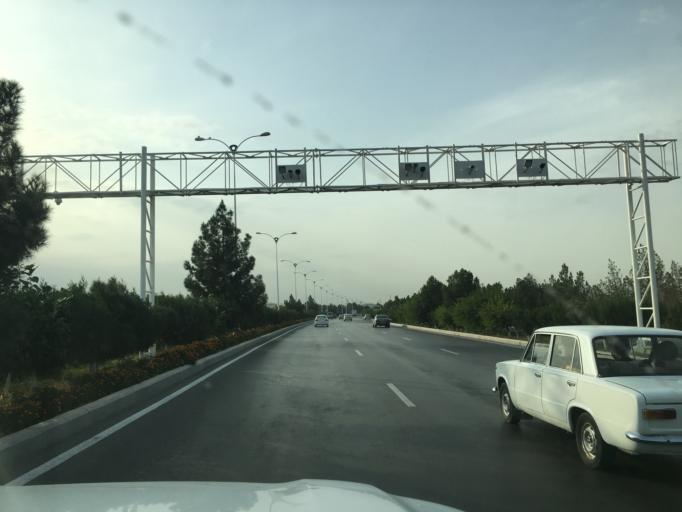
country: TM
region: Ahal
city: Annau
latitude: 37.9192
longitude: 58.4532
